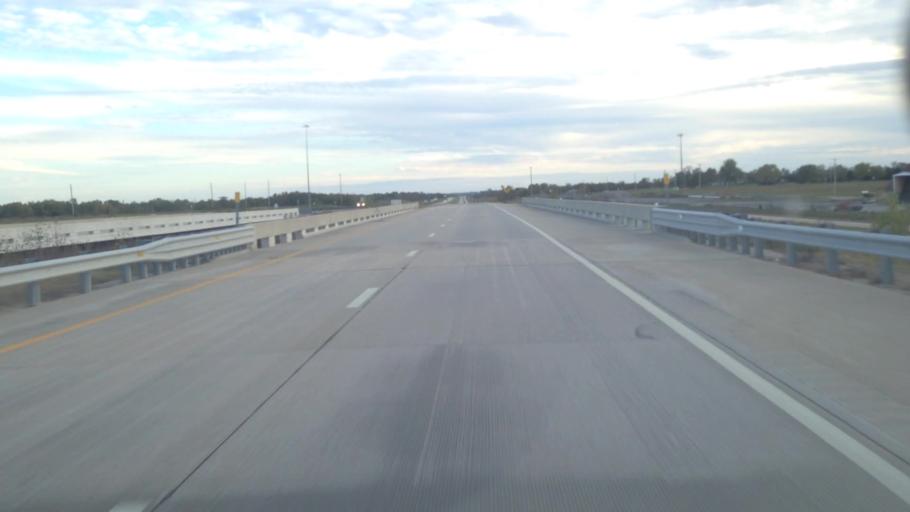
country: US
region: Kansas
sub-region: Douglas County
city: Baldwin City
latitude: 38.7830
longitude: -95.2692
